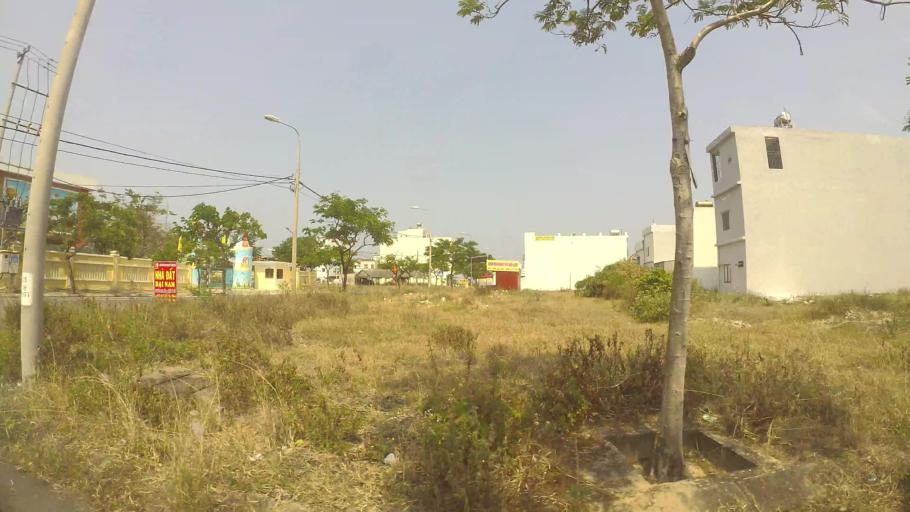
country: VN
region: Da Nang
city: Ngu Hanh Son
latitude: 15.9843
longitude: 108.2722
